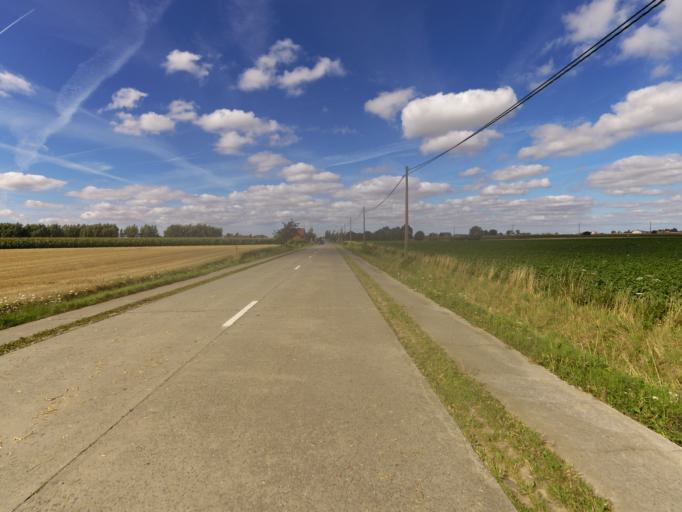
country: FR
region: Nord-Pas-de-Calais
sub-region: Departement du Nord
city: Steenvoorde
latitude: 50.8690
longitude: 2.6213
